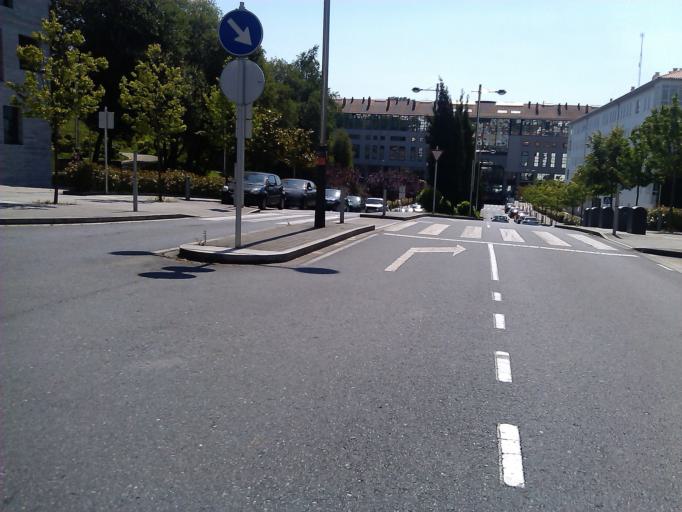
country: ES
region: Galicia
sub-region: Provincia da Coruna
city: Santiago de Compostela
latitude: 42.8837
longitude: -8.5312
